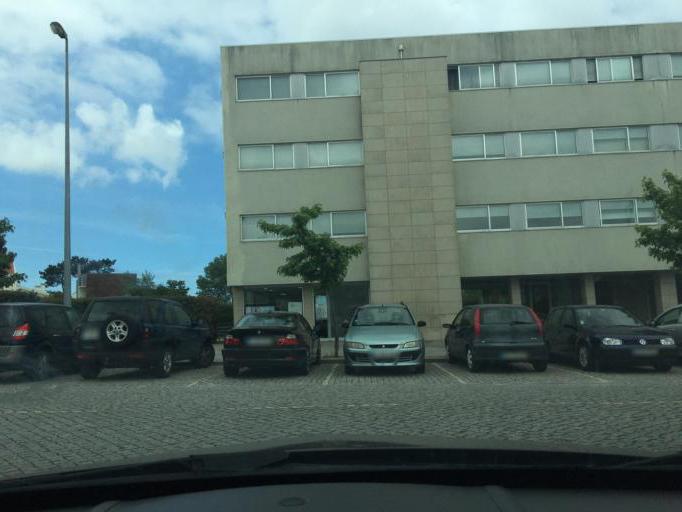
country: PT
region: Porto
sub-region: Maia
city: Gemunde
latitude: 41.2550
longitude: -8.6502
